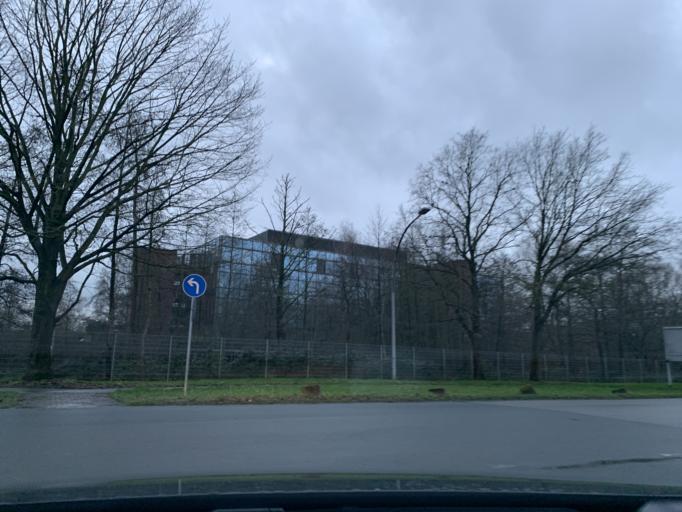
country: DE
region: Lower Saxony
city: Ritterhude
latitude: 53.1396
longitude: 8.7131
